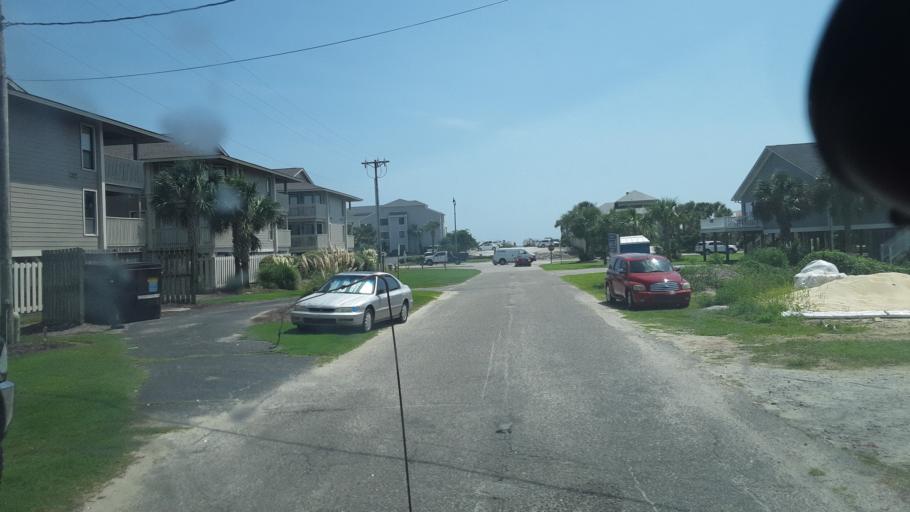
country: US
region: South Carolina
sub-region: Horry County
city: North Myrtle Beach
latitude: 33.8269
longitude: -78.6519
